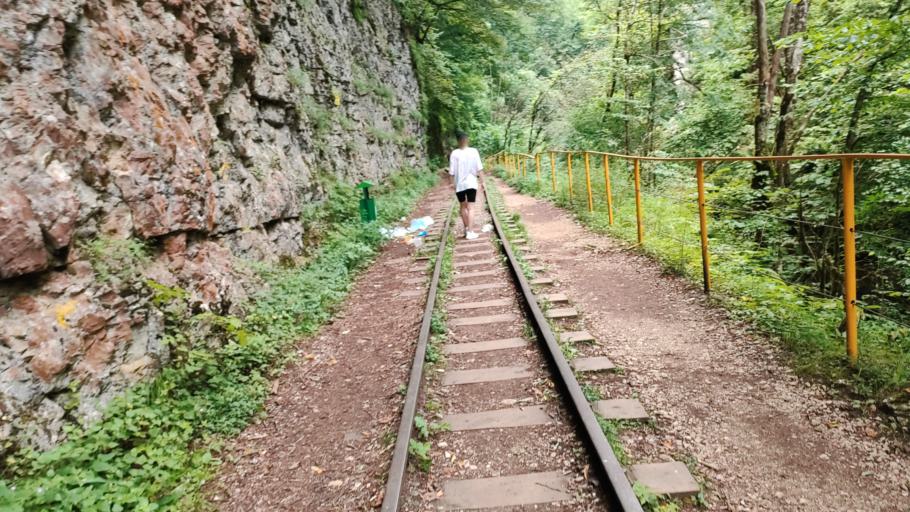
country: RU
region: Krasnodarskiy
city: Neftegorsk
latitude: 44.2091
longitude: 39.9082
